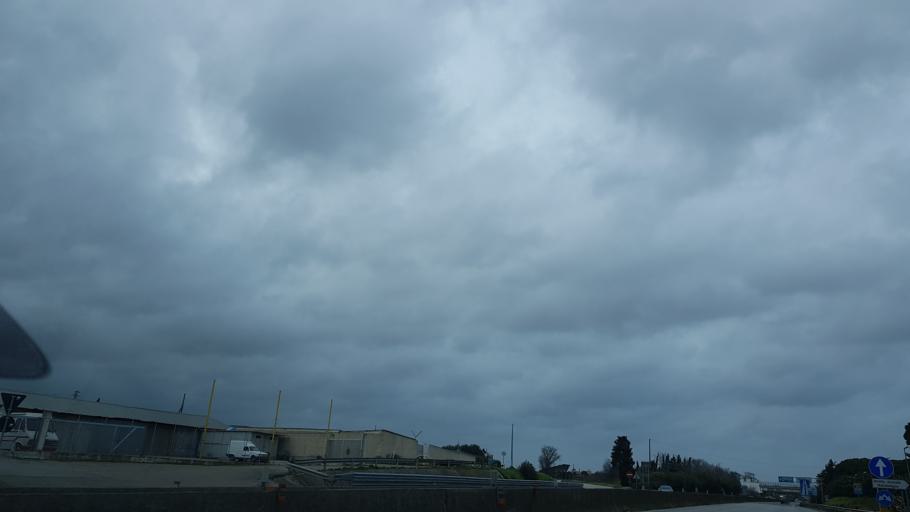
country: IT
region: Apulia
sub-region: Provincia di Brindisi
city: Brindisi
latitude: 40.6404
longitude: 17.9151
